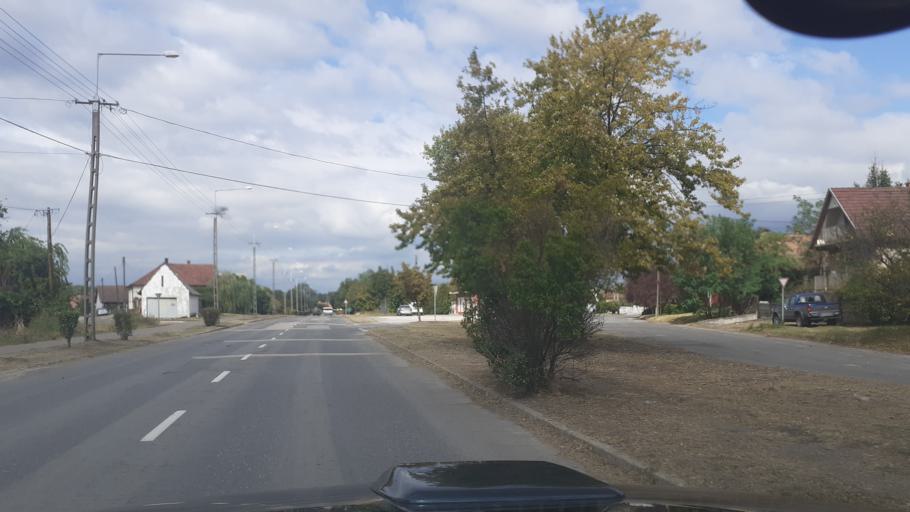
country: HU
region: Bacs-Kiskun
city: Dunavecse
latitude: 46.9105
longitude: 18.9720
